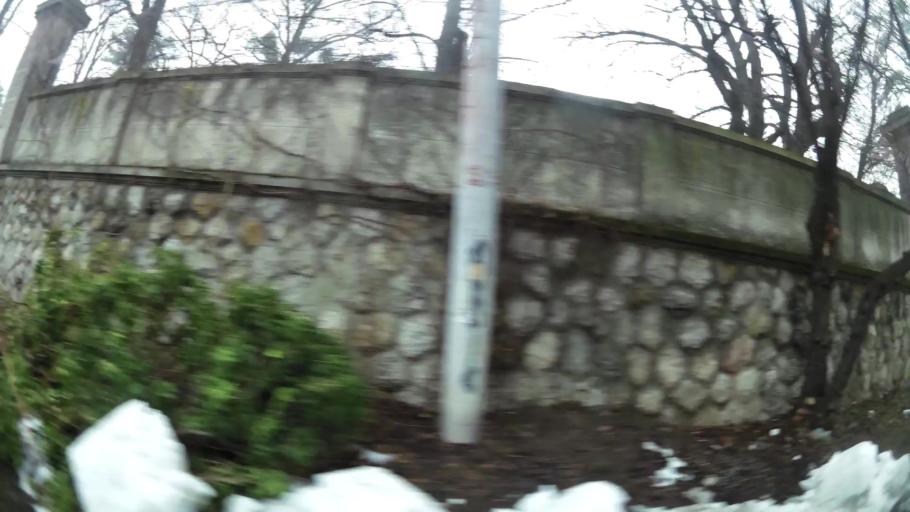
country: RS
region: Central Serbia
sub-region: Belgrade
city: Cukarica
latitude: 44.7876
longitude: 20.4363
